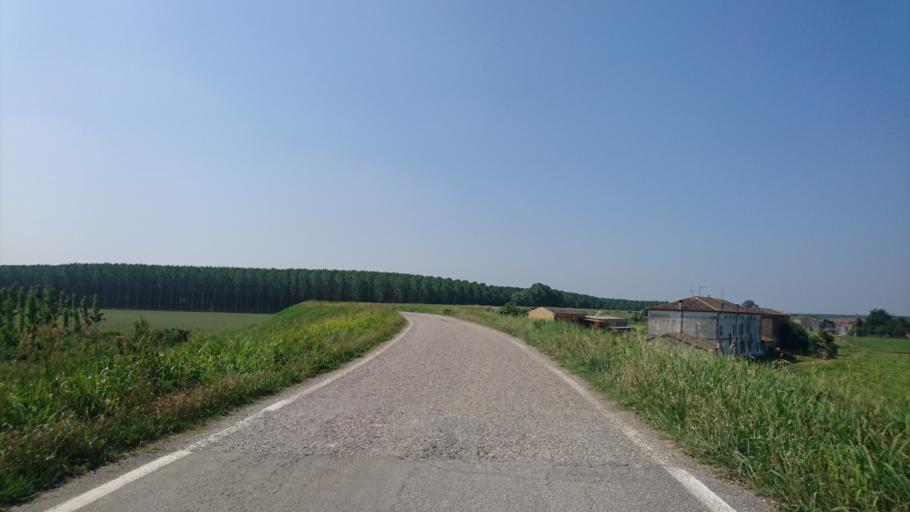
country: IT
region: Lombardy
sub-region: Provincia di Mantova
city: Serravalle a Po
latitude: 45.0685
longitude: 11.0985
